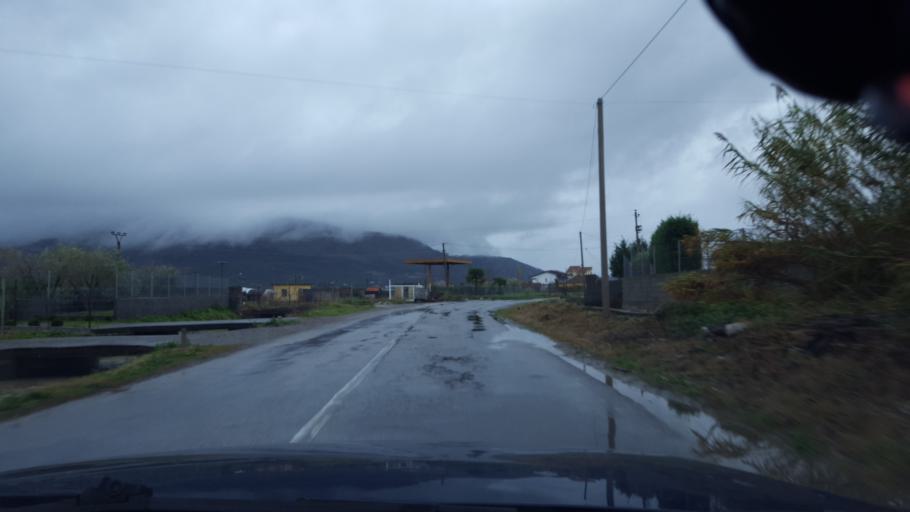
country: AL
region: Shkoder
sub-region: Rrethi i Shkodres
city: Berdica e Madhe
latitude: 42.0111
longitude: 19.4806
